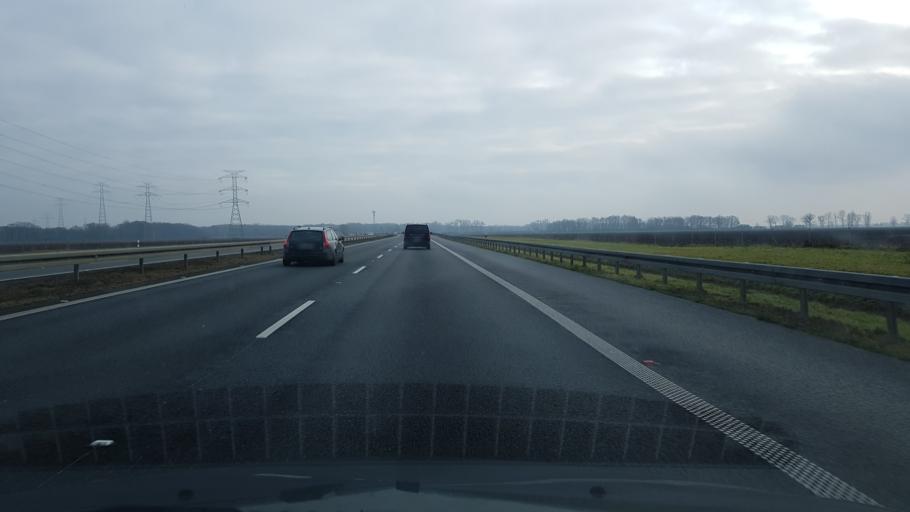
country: PL
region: Lower Silesian Voivodeship
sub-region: Powiat strzelinski
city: Wiazow
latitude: 50.8572
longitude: 17.2267
